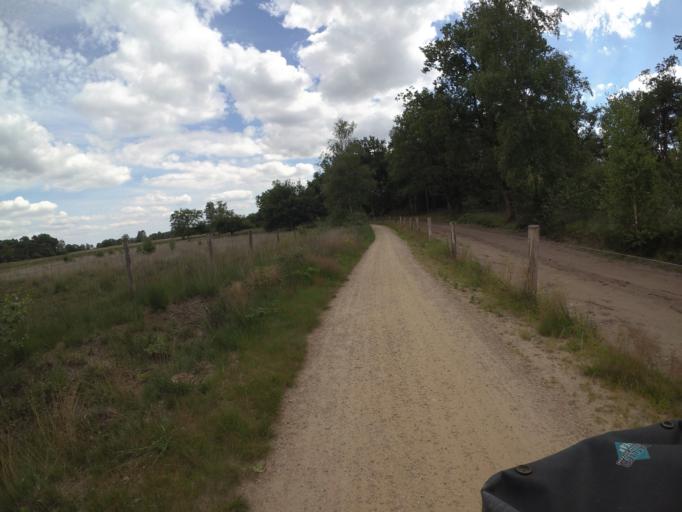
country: NL
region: North Brabant
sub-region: Gemeente Heeze-Leende
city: Heeze
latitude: 51.4030
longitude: 5.5833
